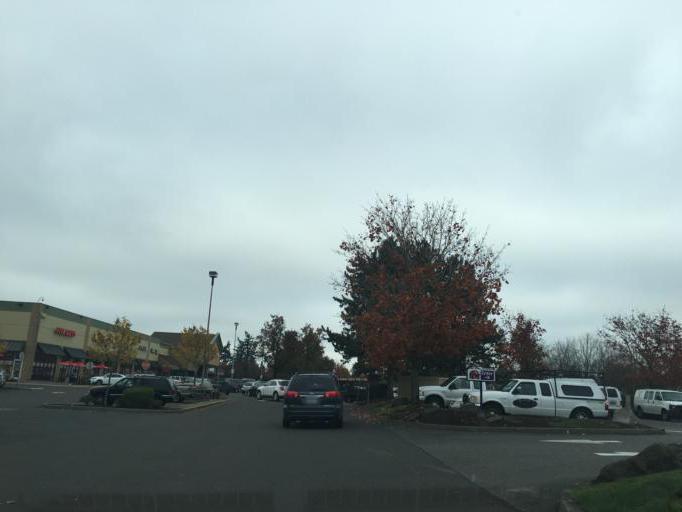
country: US
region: Oregon
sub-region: Multnomah County
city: Lents
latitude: 45.4573
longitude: -122.5799
